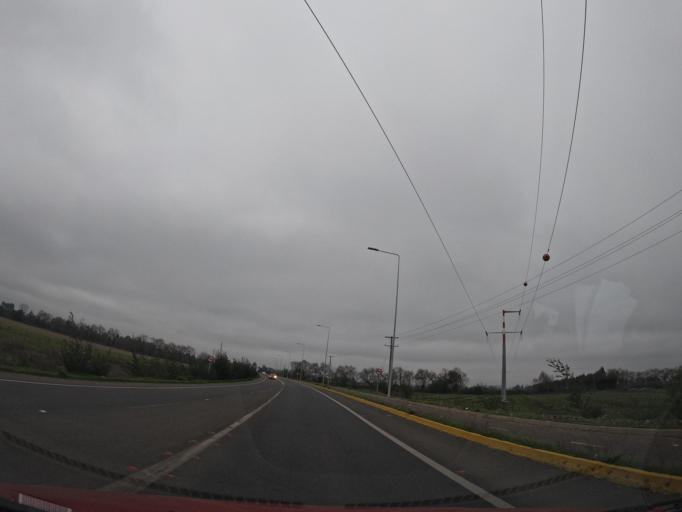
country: CL
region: Maule
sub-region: Provincia de Talca
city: San Clemente
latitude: -35.5092
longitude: -71.5133
